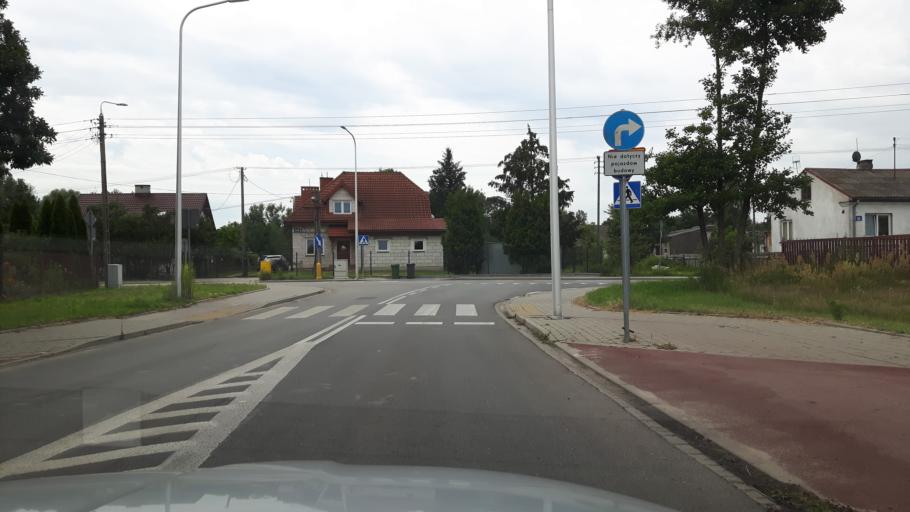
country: PL
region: Masovian Voivodeship
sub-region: Powiat wolominski
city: Kobylka
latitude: 52.3105
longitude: 21.2173
